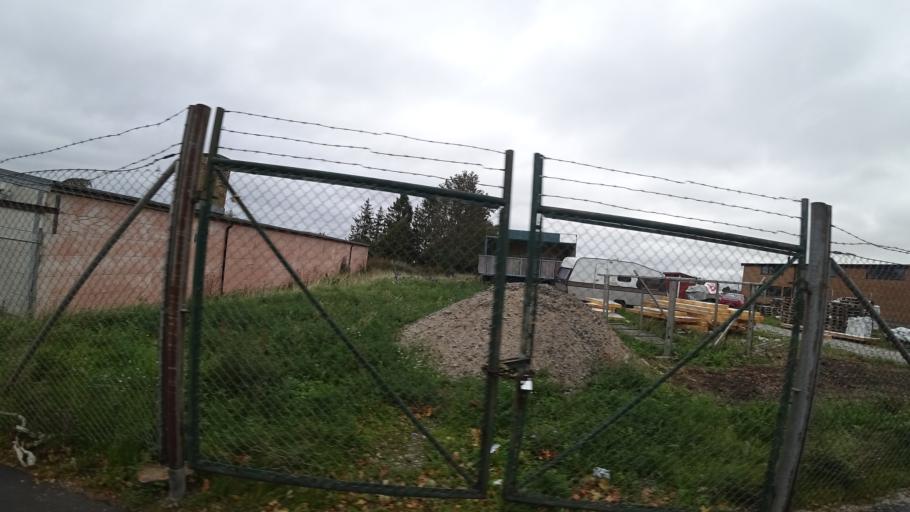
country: SE
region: Skane
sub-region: Kavlinge Kommun
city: Kaevlinge
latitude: 55.7757
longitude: 13.1030
